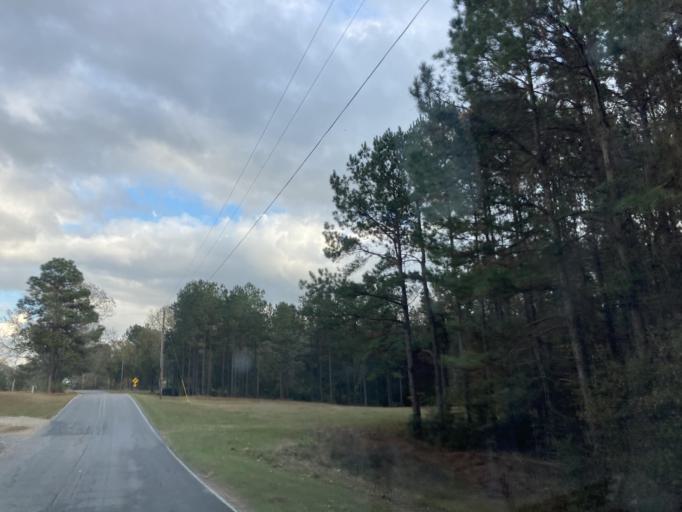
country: US
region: Mississippi
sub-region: Marion County
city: Columbia
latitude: 31.1904
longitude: -89.6700
